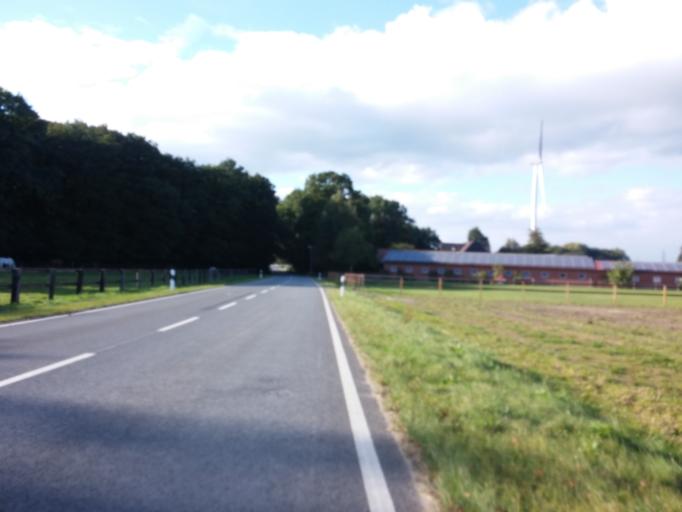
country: DE
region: North Rhine-Westphalia
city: Dorsten
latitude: 51.6188
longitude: 6.9626
